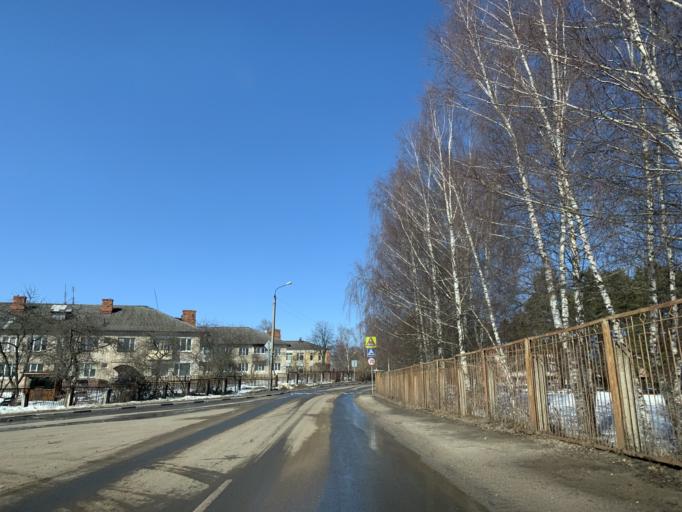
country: RU
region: Jaroslavl
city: Konstantinovskiy
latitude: 57.8402
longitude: 39.5805
